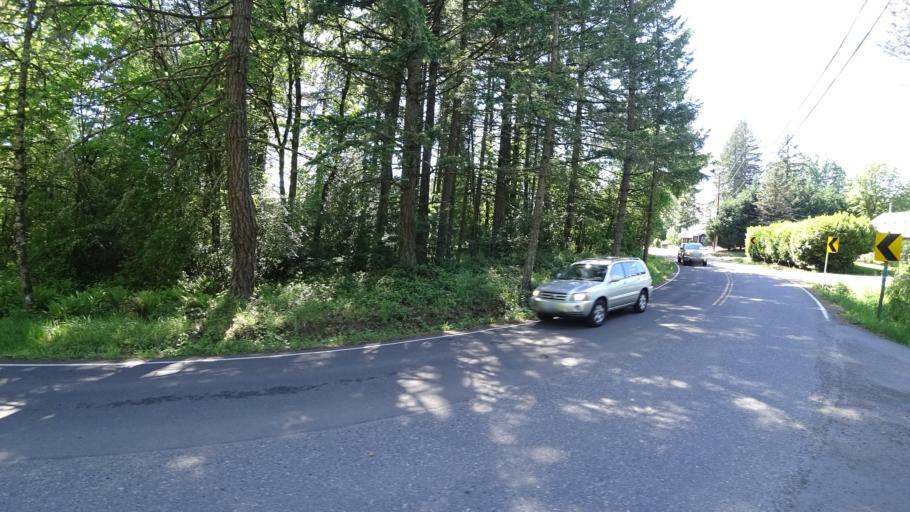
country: US
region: Oregon
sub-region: Washington County
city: Cedar Mill
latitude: 45.5541
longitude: -122.7962
